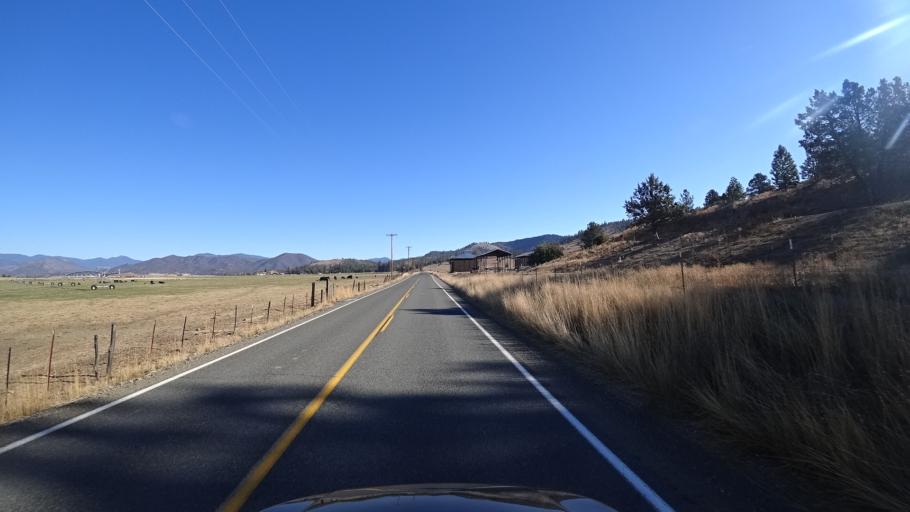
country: US
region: California
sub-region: Siskiyou County
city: Yreka
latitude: 41.5358
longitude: -122.8360
